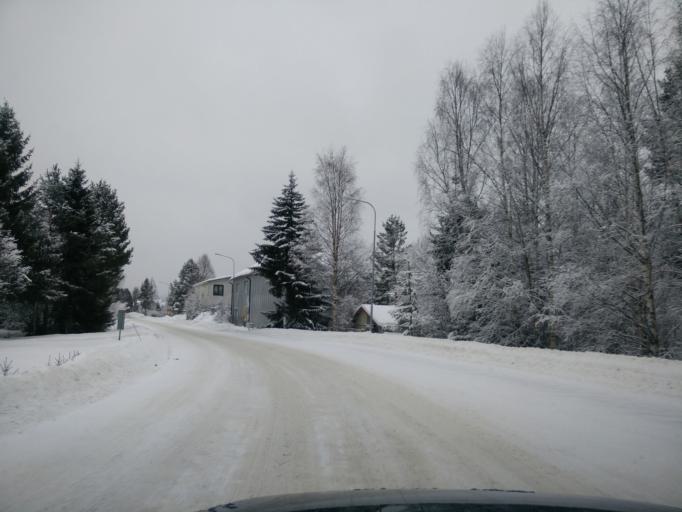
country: SE
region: Vaesternorrland
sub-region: Ange Kommun
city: Ange
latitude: 62.4937
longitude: 15.4723
